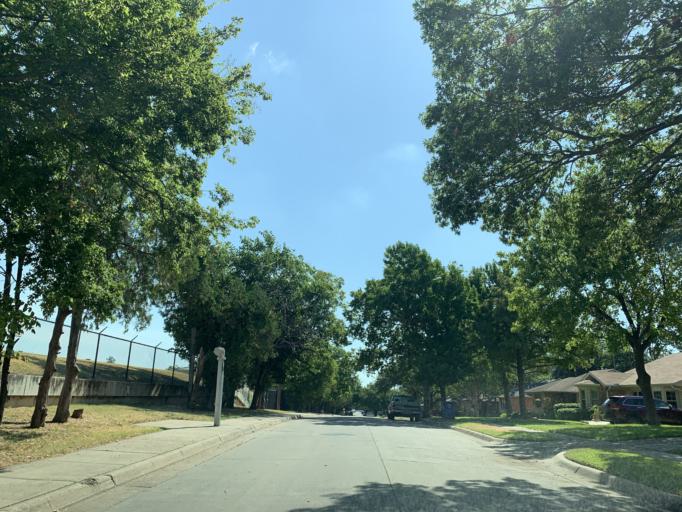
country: US
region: Texas
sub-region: Dallas County
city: Cockrell Hill
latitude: 32.7422
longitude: -96.8633
